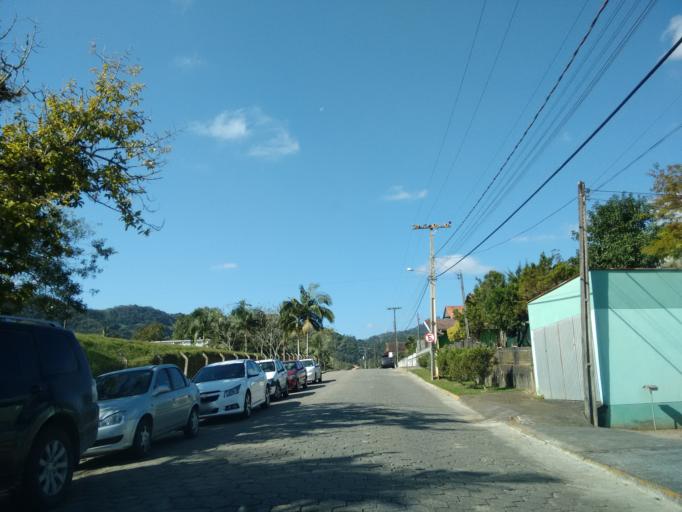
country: BR
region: Santa Catarina
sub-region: Pomerode
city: Pomerode
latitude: -26.7387
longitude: -49.1717
